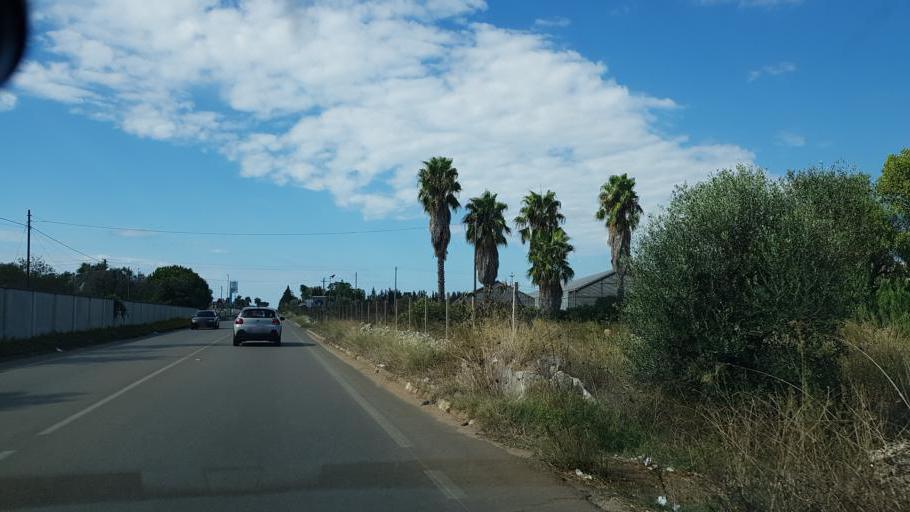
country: IT
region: Apulia
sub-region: Provincia di Lecce
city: Leverano
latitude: 40.2836
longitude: 17.9599
